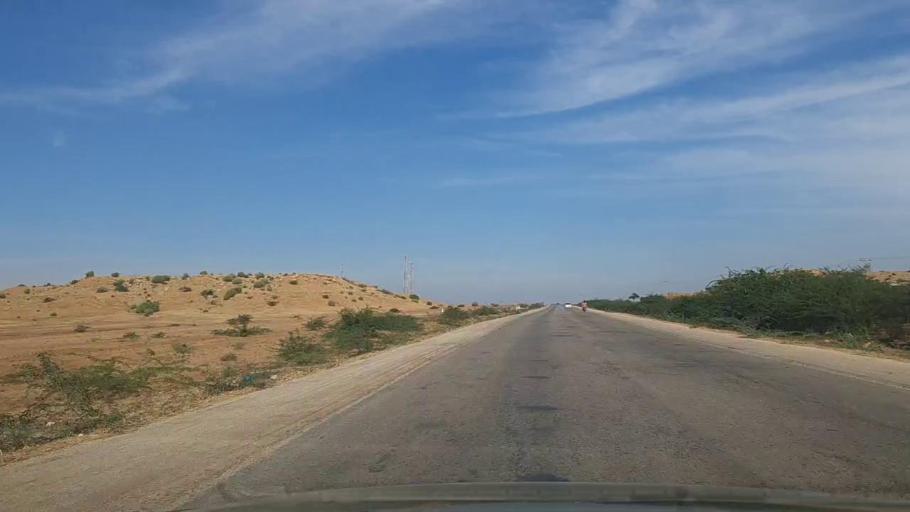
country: PK
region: Sindh
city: Bulri
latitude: 25.0462
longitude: 68.2433
